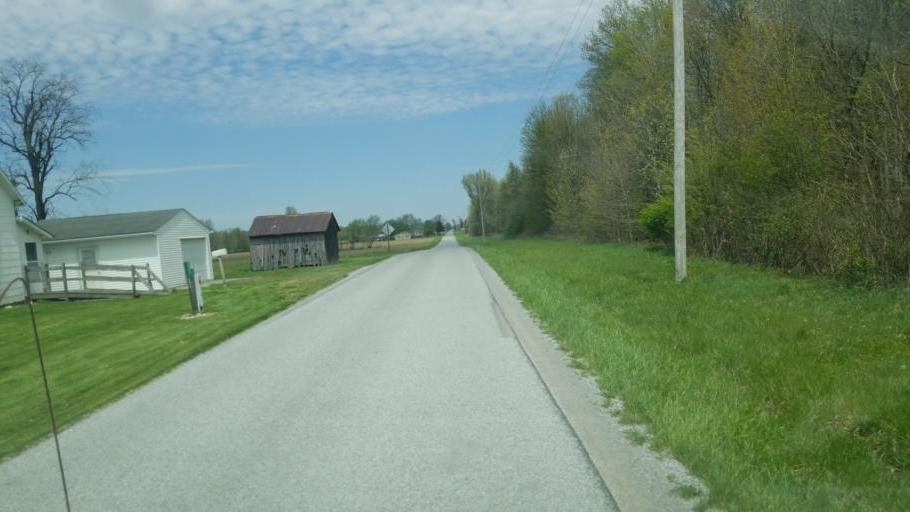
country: US
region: Ohio
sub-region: Hardin County
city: Ada
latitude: 40.7979
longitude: -83.8990
